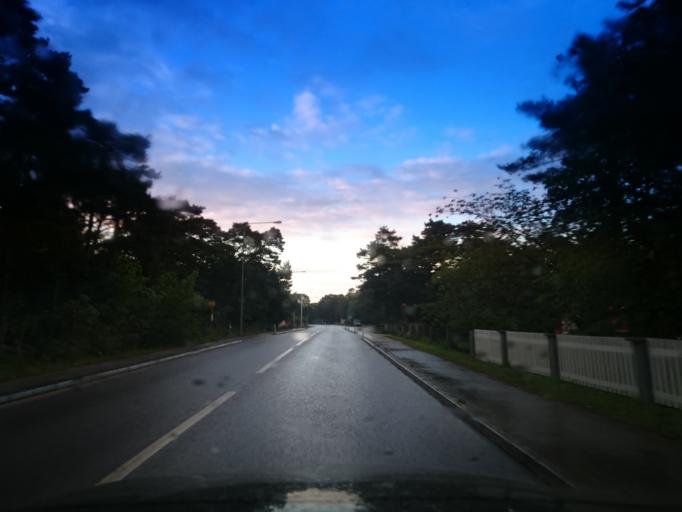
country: SE
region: Gotland
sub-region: Gotland
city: Visby
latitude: 57.6609
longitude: 18.3303
